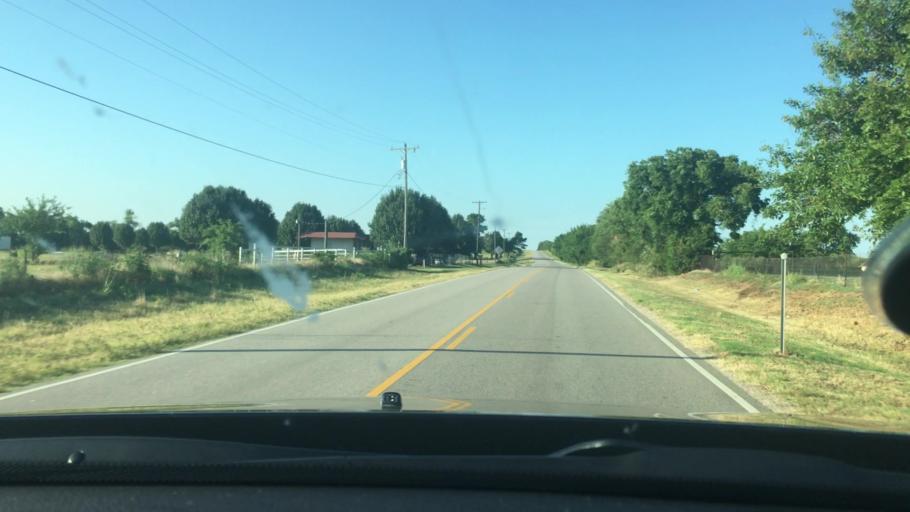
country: US
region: Oklahoma
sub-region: Murray County
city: Sulphur
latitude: 34.6157
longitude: -96.8448
